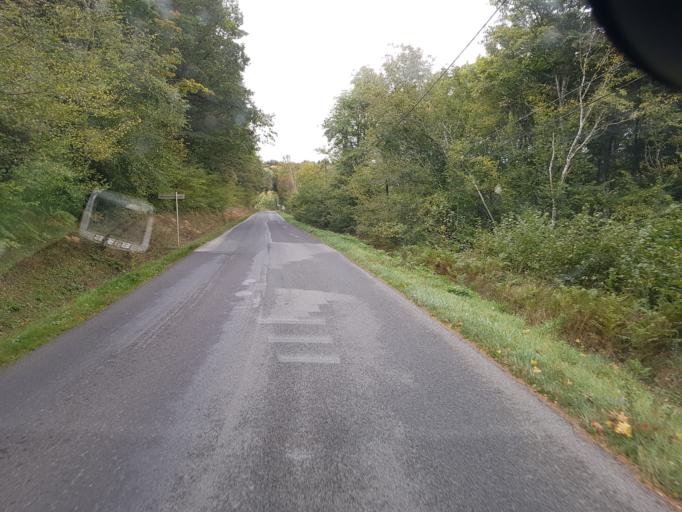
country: FR
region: Languedoc-Roussillon
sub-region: Departement de l'Aude
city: Cuxac-Cabardes
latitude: 43.4220
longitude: 2.3103
